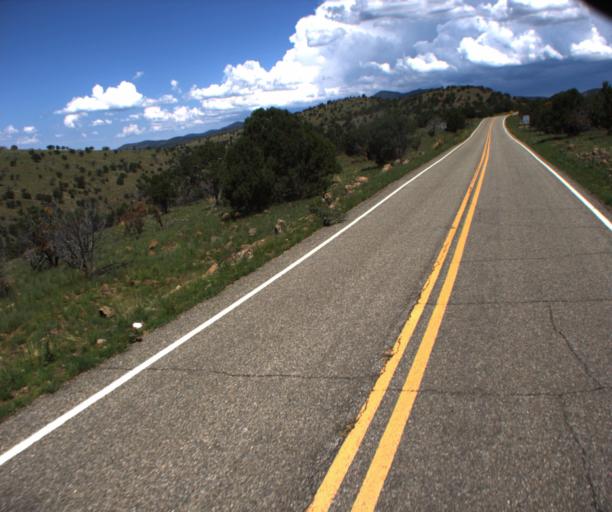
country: US
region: Arizona
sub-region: Greenlee County
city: Morenci
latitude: 33.3424
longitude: -109.3466
